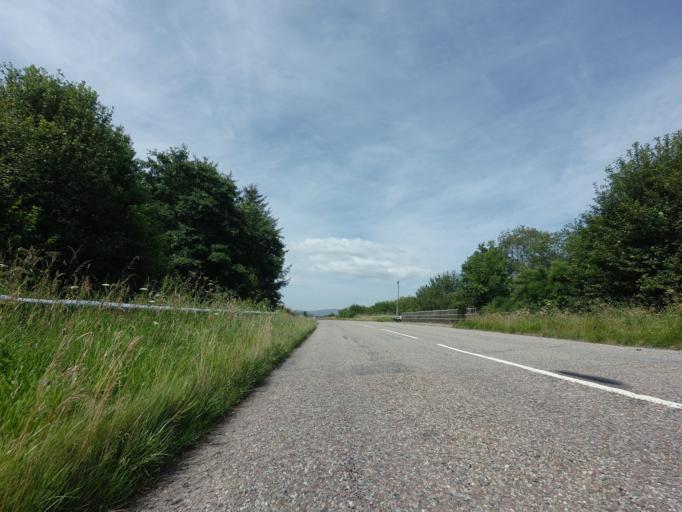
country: GB
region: Scotland
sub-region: Highland
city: Tain
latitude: 57.8370
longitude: -4.1842
